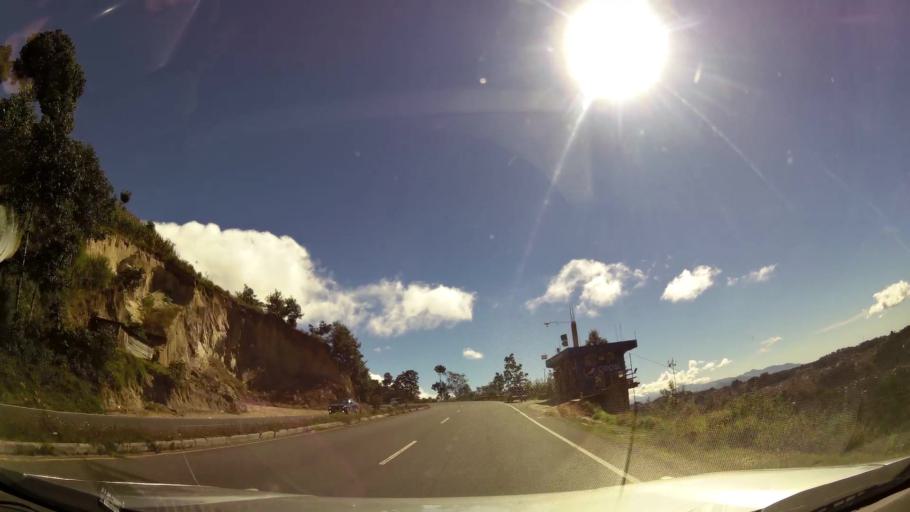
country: GT
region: Solola
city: Solola
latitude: 14.8275
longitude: -91.1860
